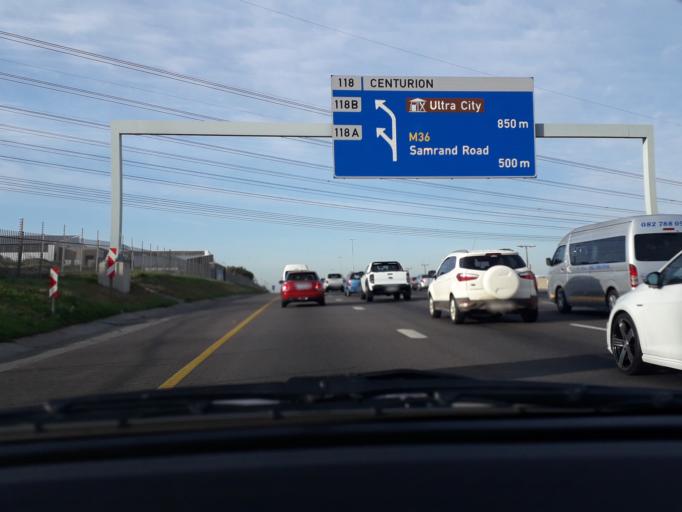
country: ZA
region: Gauteng
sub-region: City of Tshwane Metropolitan Municipality
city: Centurion
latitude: -25.9192
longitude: 28.1513
